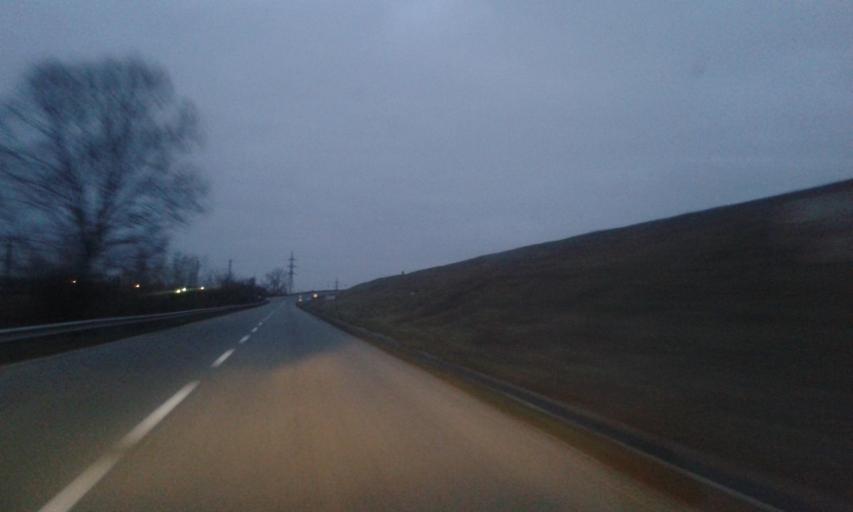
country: RO
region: Gorj
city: Targu Jiu
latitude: 45.0610
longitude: 23.2736
